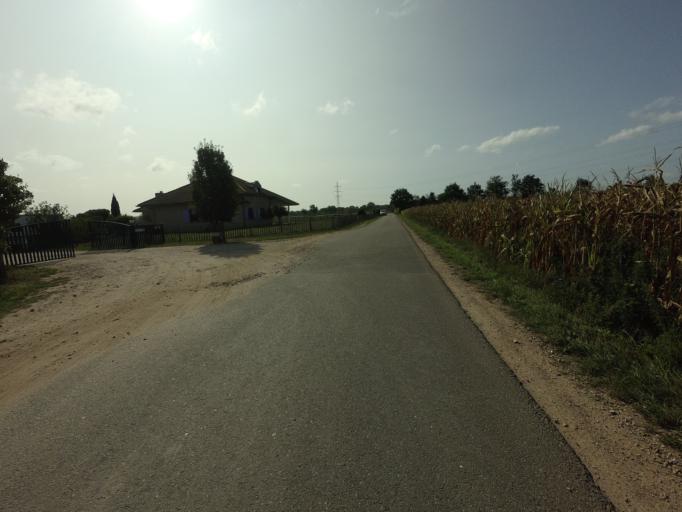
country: NL
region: Limburg
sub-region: Gemeente Roerdalen
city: Herkenbosch
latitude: 51.1960
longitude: 6.0617
